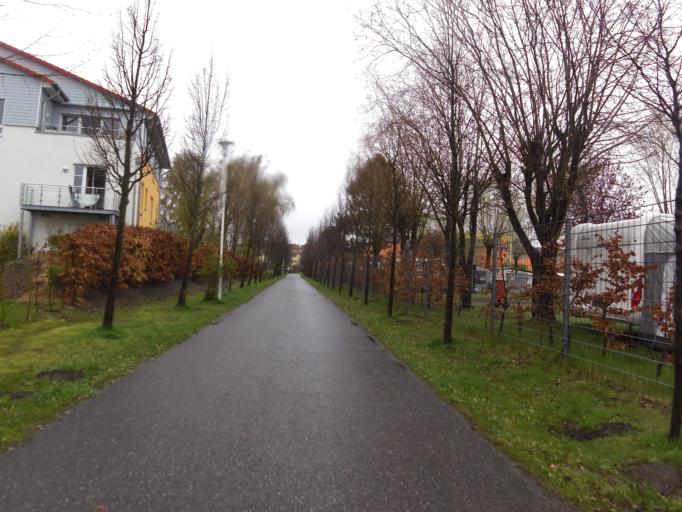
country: DE
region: Mecklenburg-Vorpommern
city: Zingst
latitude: 54.4388
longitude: 12.7054
